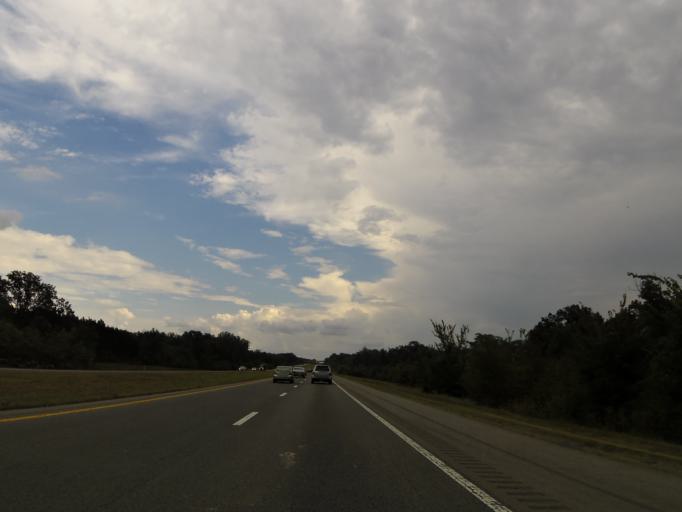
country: US
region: Tennessee
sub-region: Rutherford County
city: Smyrna
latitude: 35.9615
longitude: -86.4470
